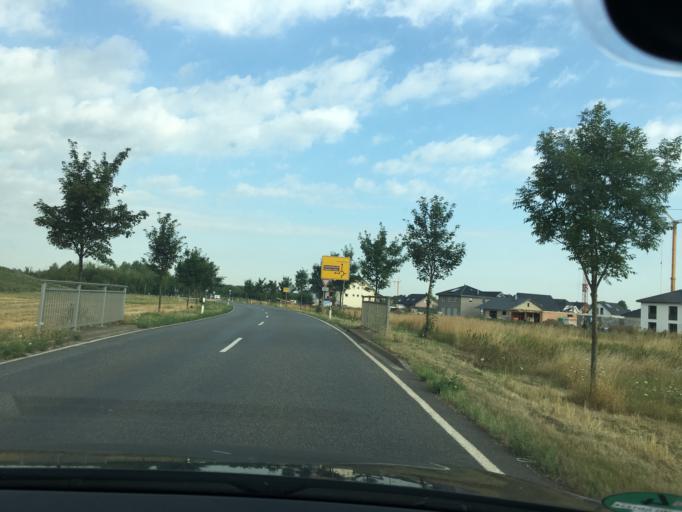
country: DE
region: North Rhine-Westphalia
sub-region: Regierungsbezirk Koln
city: Inden
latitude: 50.8702
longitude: 6.4034
